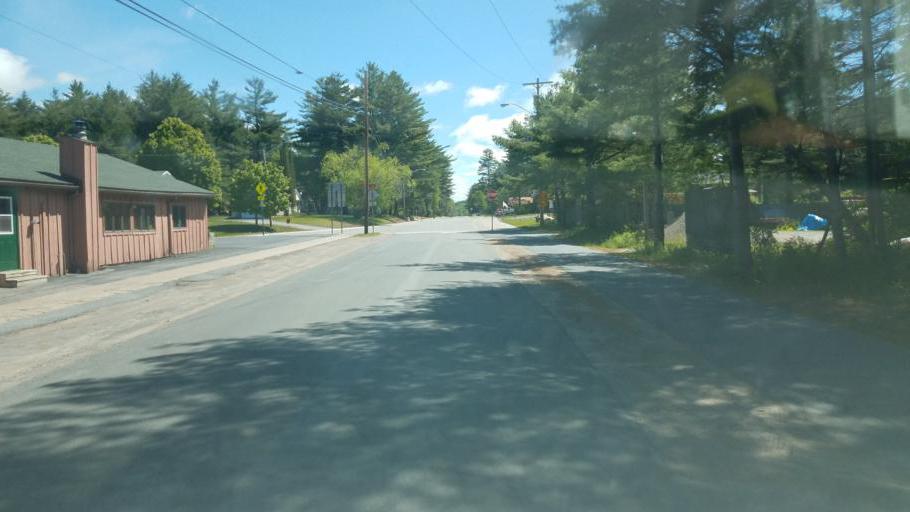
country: US
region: New York
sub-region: Oneida County
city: Boonville
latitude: 43.6999
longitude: -75.0012
